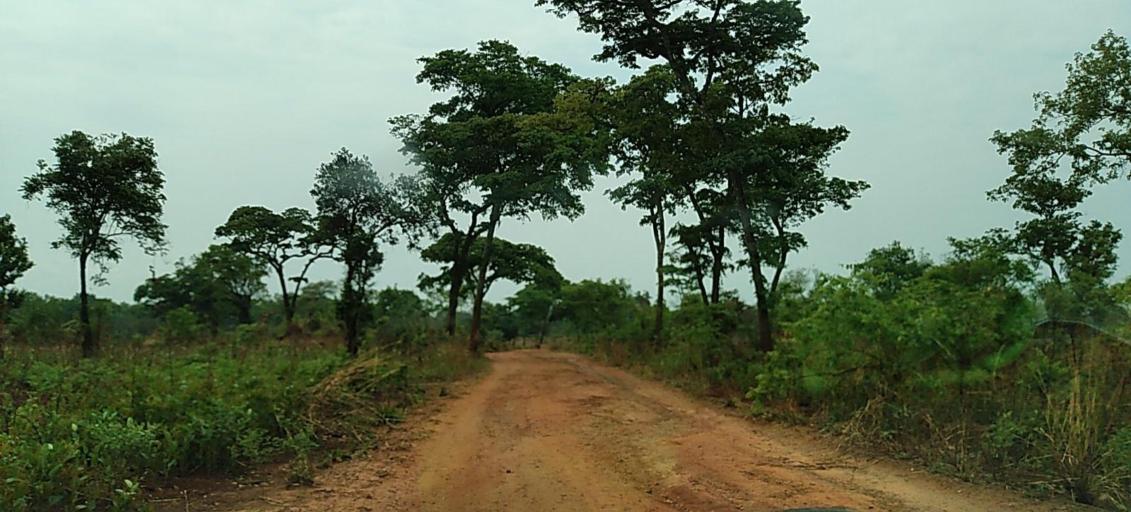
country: ZM
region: North-Western
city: Solwezi
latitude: -12.3371
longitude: 26.5239
